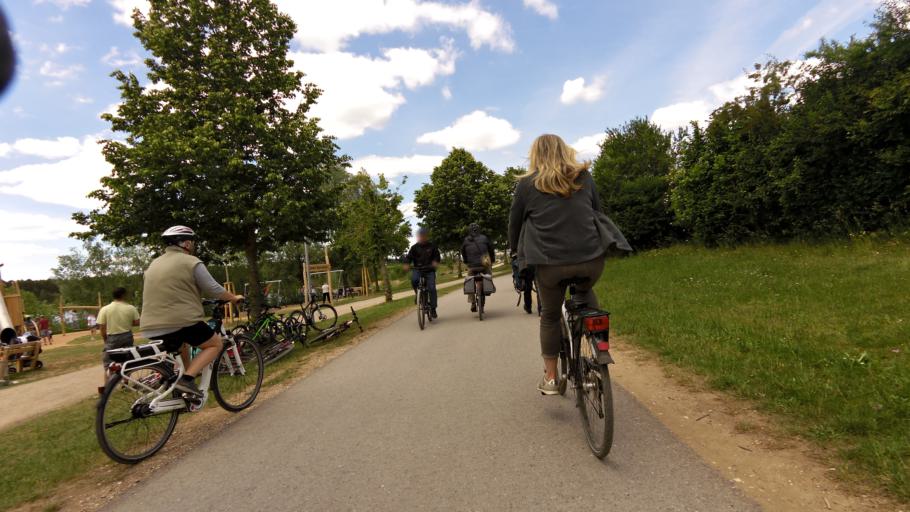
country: DE
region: Bavaria
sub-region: Regierungsbezirk Mittelfranken
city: Spalt
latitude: 49.1437
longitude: 10.9149
